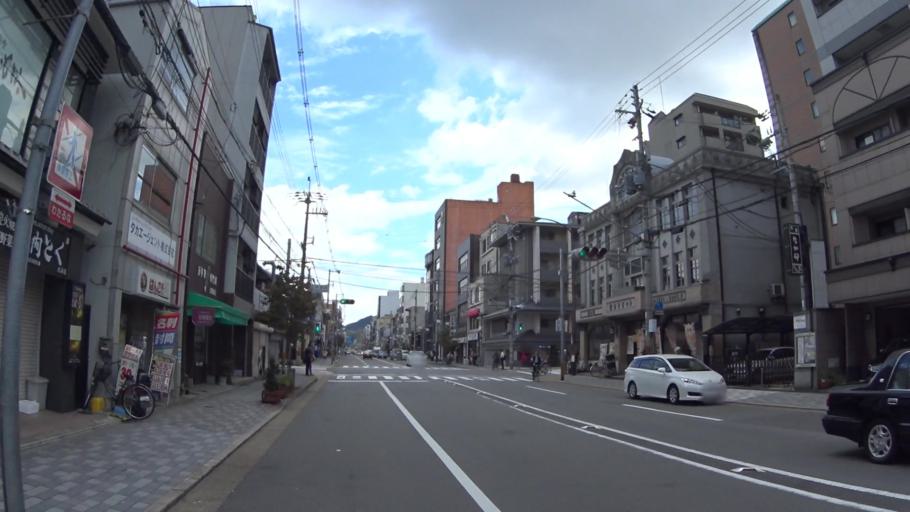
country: JP
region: Kyoto
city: Kyoto
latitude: 34.9893
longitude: 135.7563
